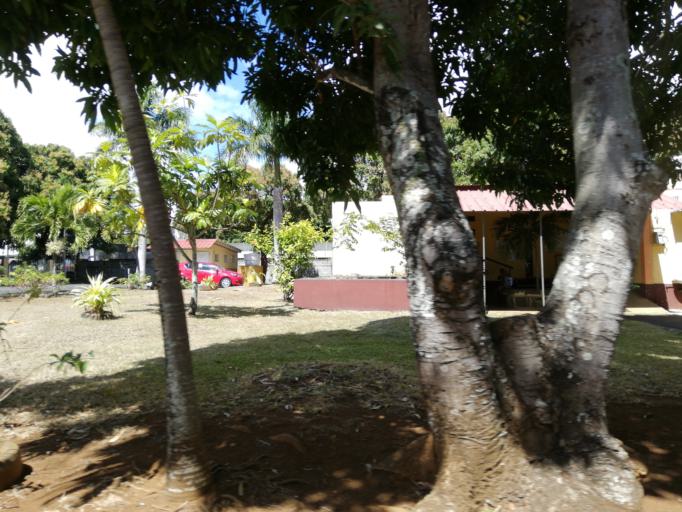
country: MU
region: Plaines Wilhems
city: Ebene
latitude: -20.2274
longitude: 57.4631
